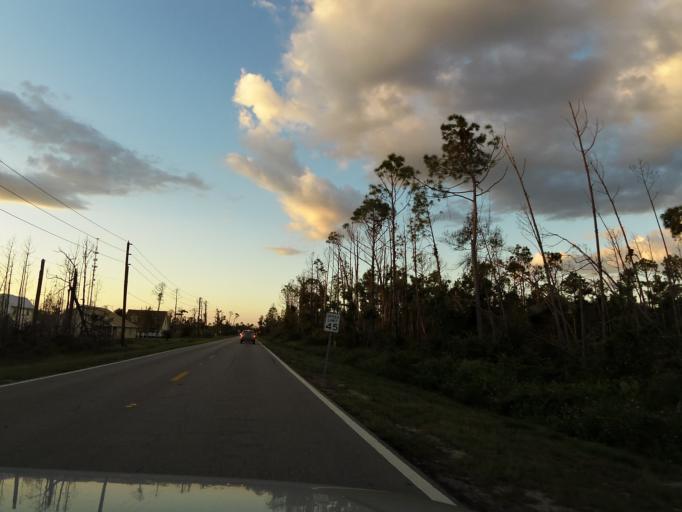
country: US
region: Florida
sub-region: Bay County
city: Mexico Beach
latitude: 29.9386
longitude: -85.3887
